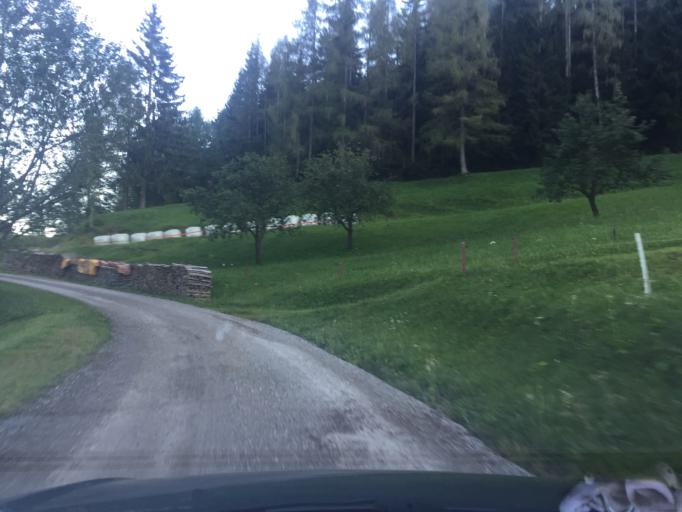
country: SI
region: Ravne na Koroskem
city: Kotlje
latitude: 46.4636
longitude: 14.9900
